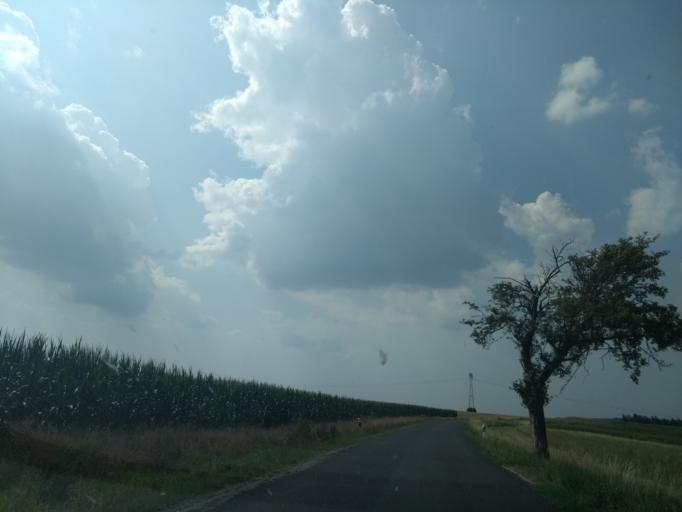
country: DE
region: Thuringia
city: Eisenberg
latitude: 50.9811
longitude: 11.9256
